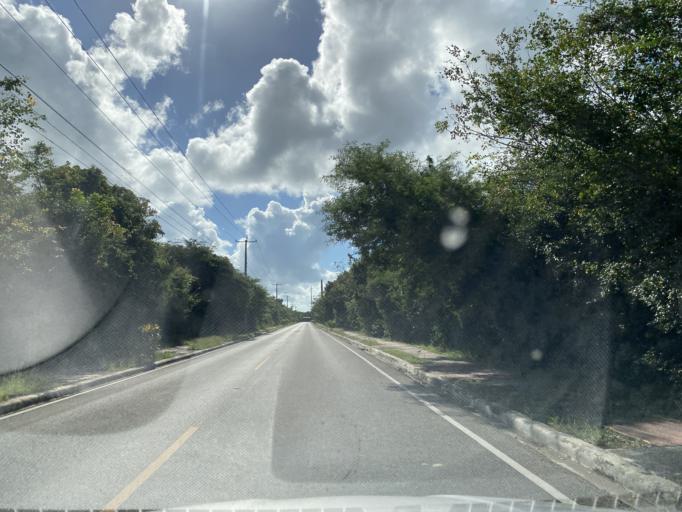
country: DO
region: La Altagracia
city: San Rafael del Yuma
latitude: 18.3365
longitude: -68.8099
